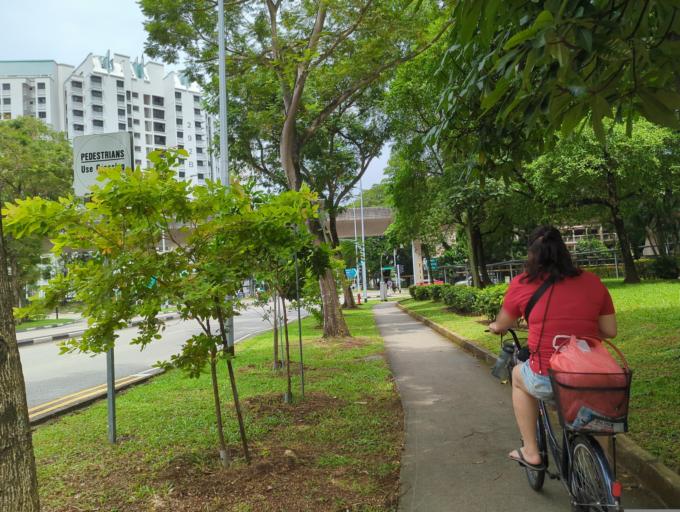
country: MY
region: Johor
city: Kampung Pasir Gudang Baru
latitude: 1.3943
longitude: 103.8989
